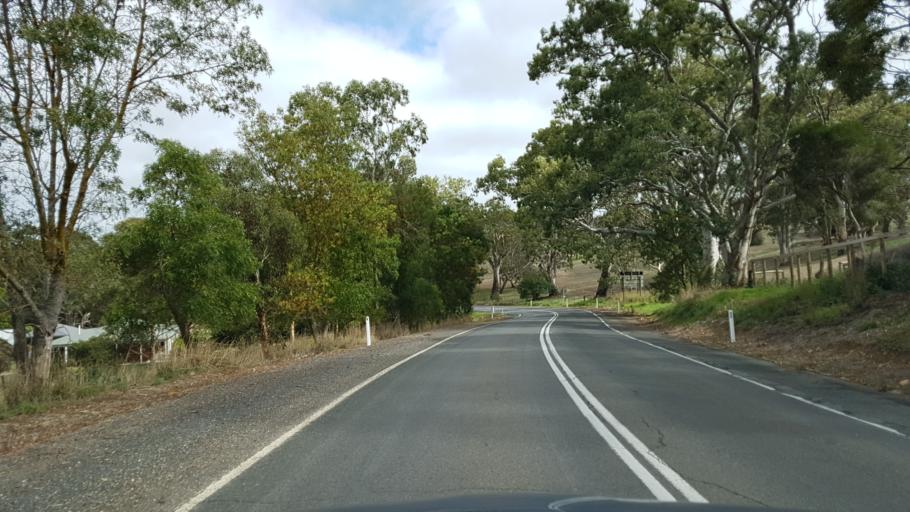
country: AU
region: South Australia
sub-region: Mount Barker
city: Nairne
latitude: -35.0404
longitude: 138.9256
